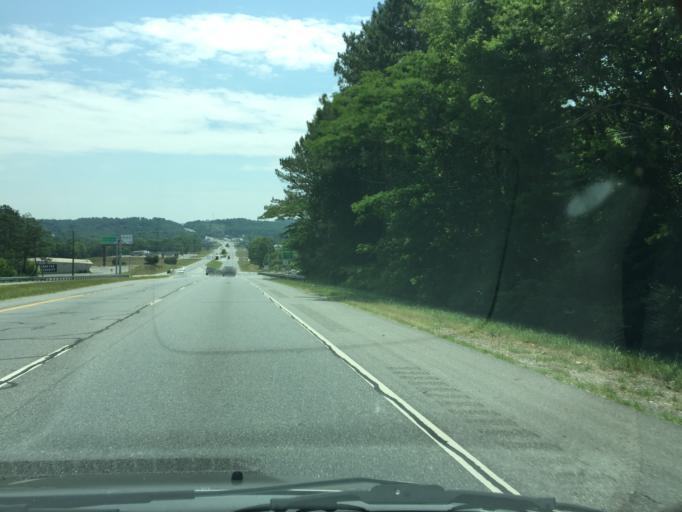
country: US
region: Georgia
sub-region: Catoosa County
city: Indian Springs
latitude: 34.9347
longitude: -85.1949
